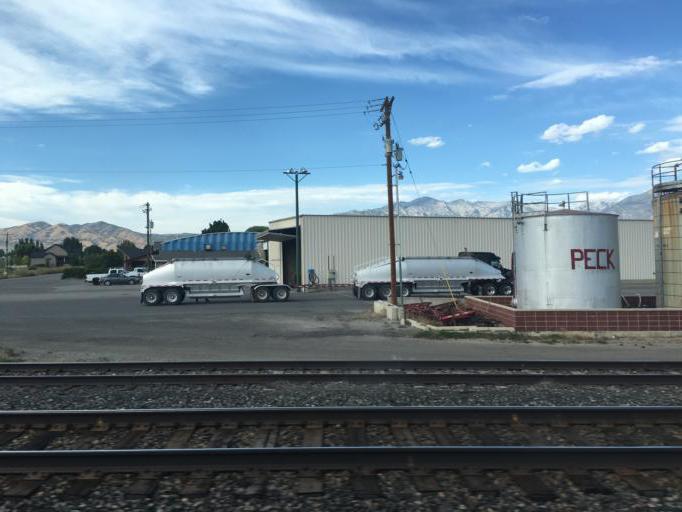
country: US
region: Utah
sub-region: Utah County
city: Lehi
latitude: 40.3788
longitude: -111.8395
